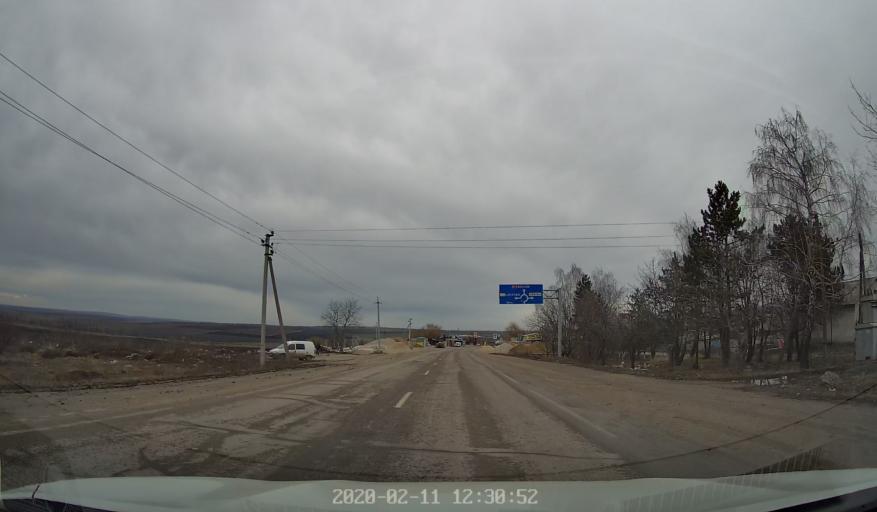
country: MD
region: Raionul Edinet
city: Edinet
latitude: 48.1689
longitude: 27.2801
